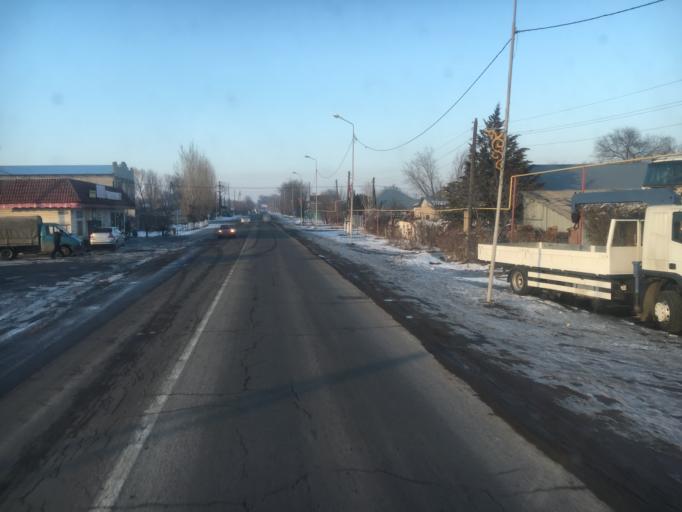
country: KZ
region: Almaty Oblysy
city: Burunday
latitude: 43.3693
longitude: 76.6414
